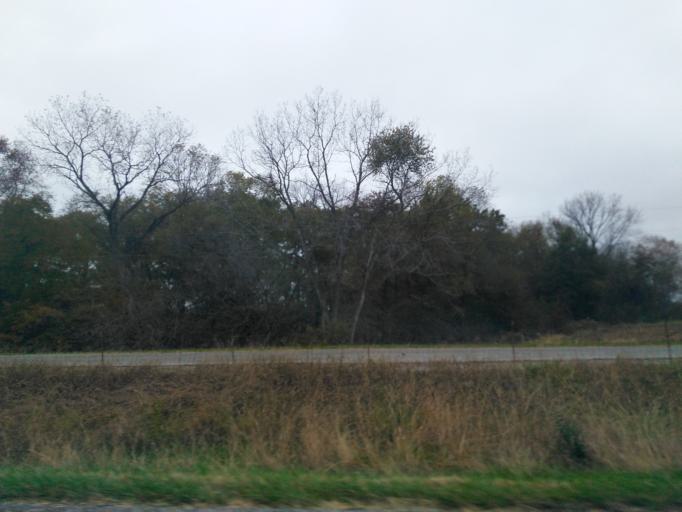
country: US
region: Illinois
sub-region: Madison County
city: Highland
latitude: 38.8235
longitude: -89.5569
